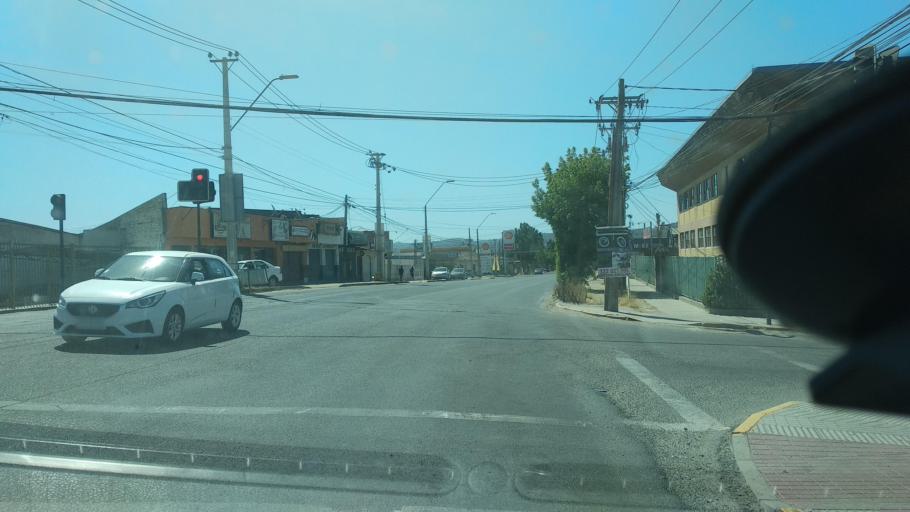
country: CL
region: Valparaiso
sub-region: Provincia de Marga Marga
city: Villa Alemana
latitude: -33.0466
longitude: -71.3532
